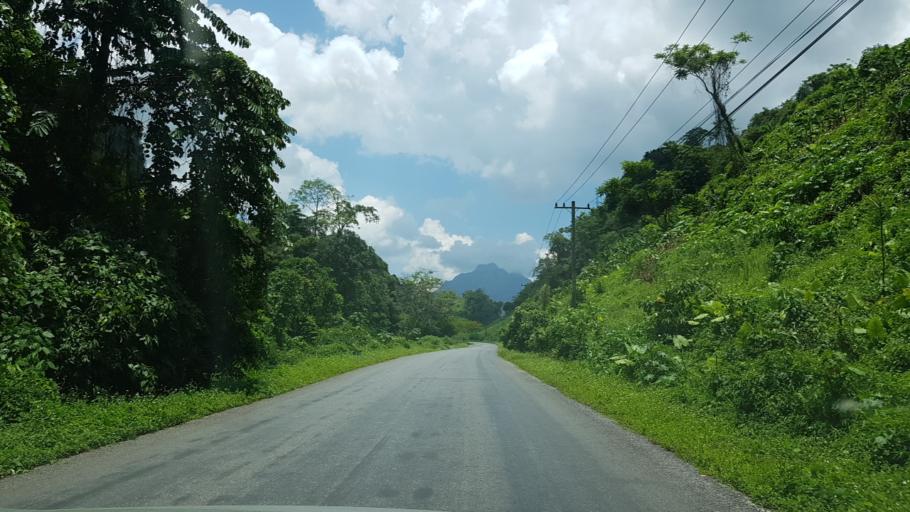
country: LA
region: Vientiane
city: Muang Kasi
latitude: 19.1389
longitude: 102.2963
